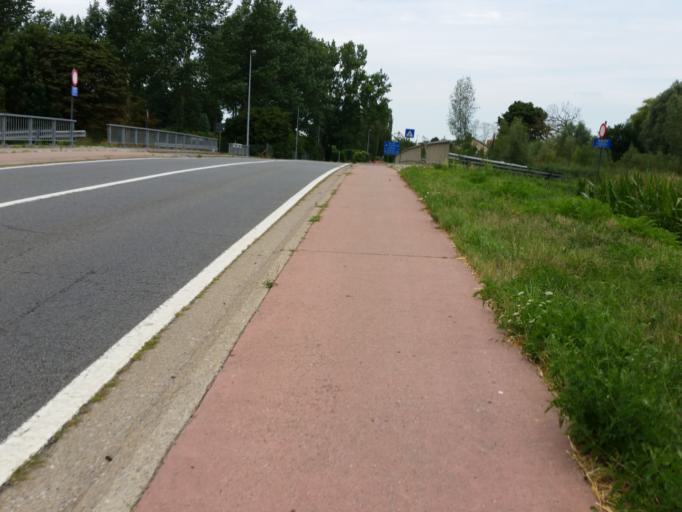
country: BE
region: Flanders
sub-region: Provincie Vlaams-Brabant
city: Zemst
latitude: 50.9757
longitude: 4.4613
